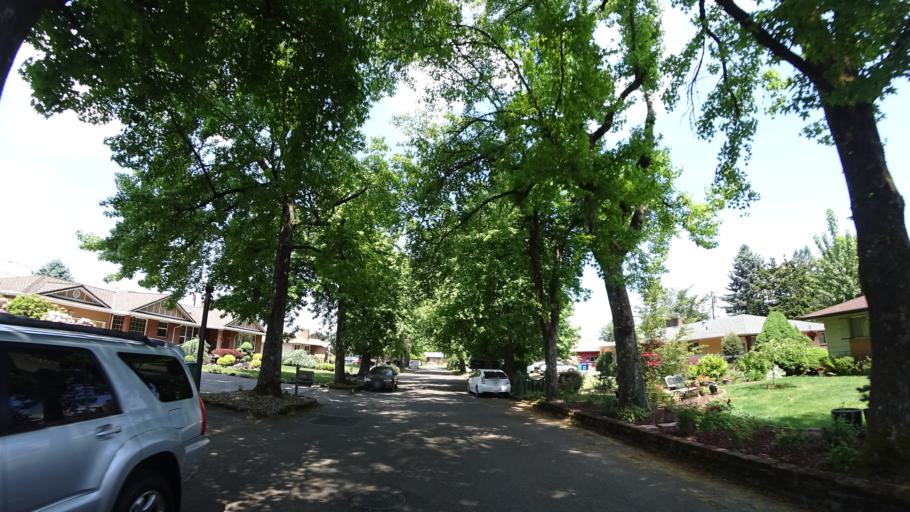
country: US
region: Oregon
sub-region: Multnomah County
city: Fairview
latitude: 45.5343
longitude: -122.5060
